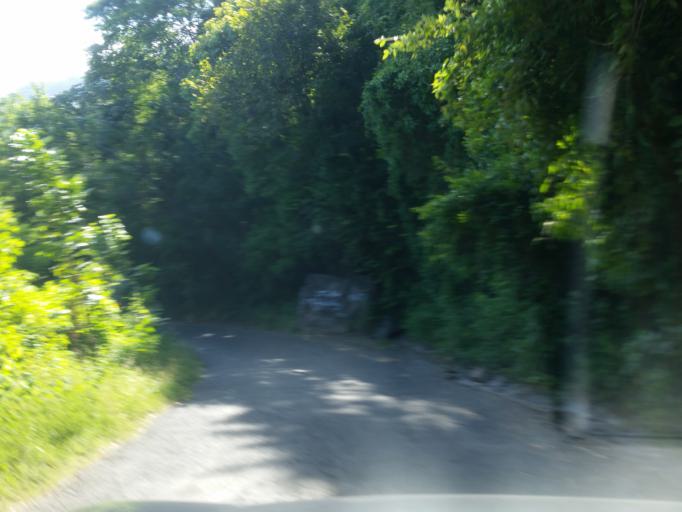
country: NI
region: Masaya
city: Catarina
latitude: 11.9404
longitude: -86.0540
